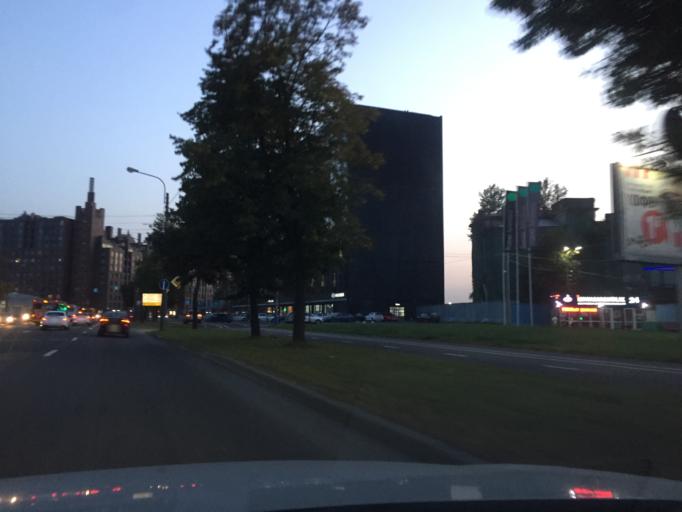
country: RU
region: Leningrad
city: Kalininskiy
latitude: 59.9607
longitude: 30.4076
